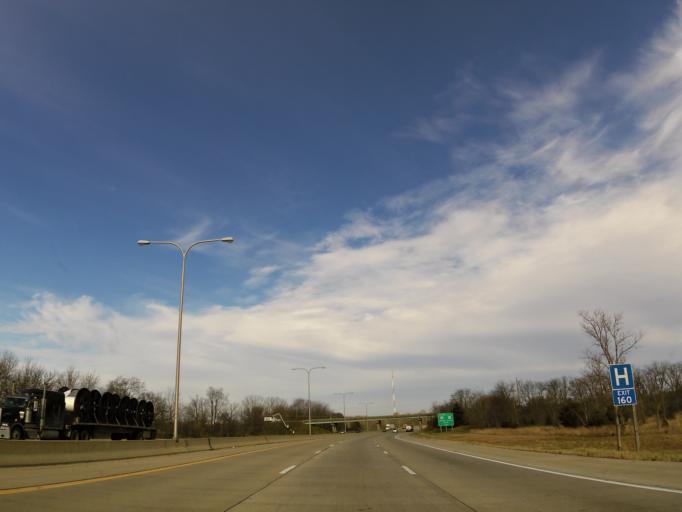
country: US
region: Illinois
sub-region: McLean County
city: Bloomington
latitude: 40.4640
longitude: -89.0300
